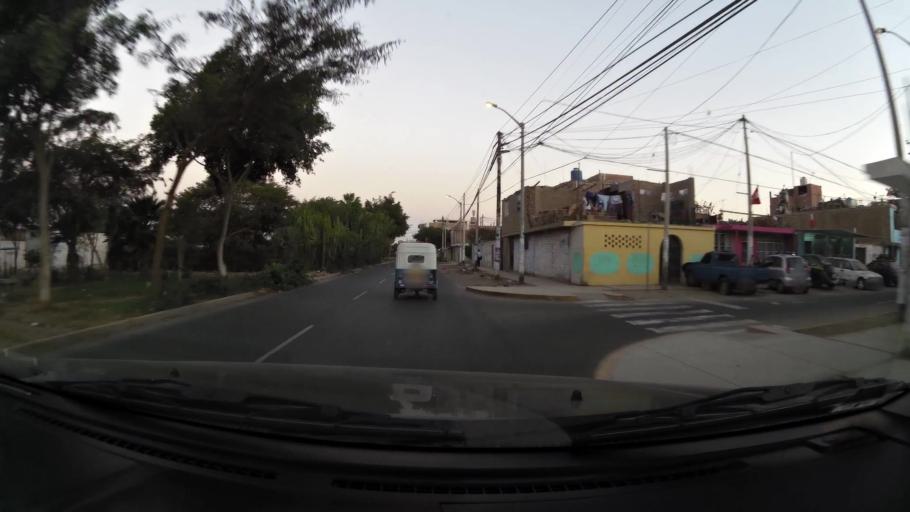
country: PE
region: Ica
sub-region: Provincia de Ica
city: Ica
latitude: -14.0790
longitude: -75.7321
